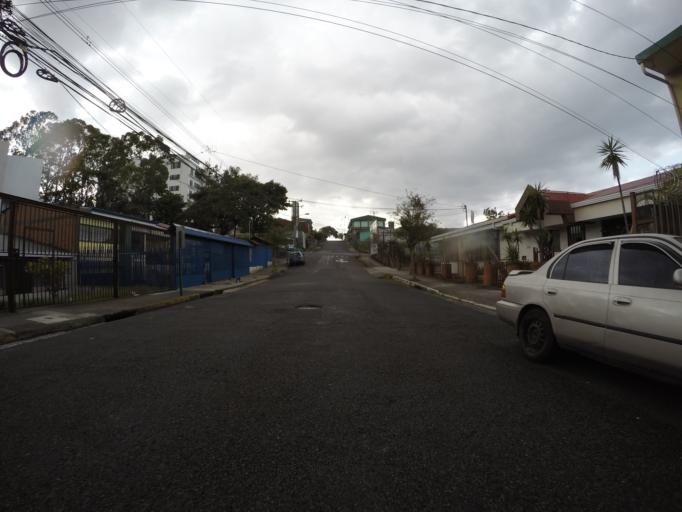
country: CR
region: San Jose
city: Calle Blancos
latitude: 9.9390
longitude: -84.0655
